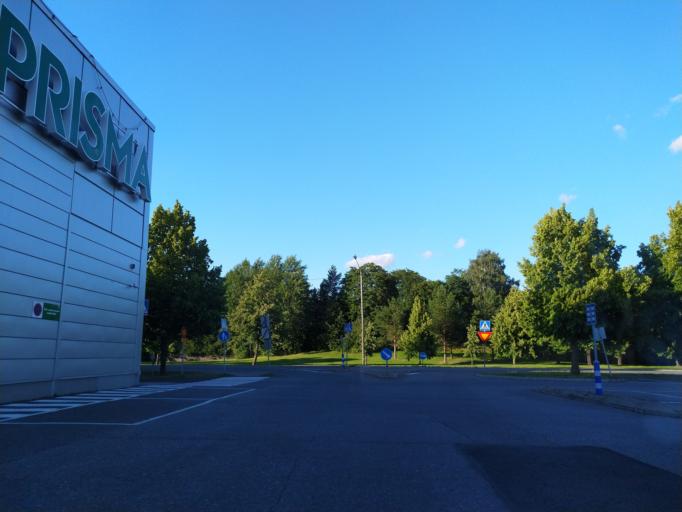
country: FI
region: Varsinais-Suomi
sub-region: Turku
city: Turku
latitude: 60.4461
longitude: 22.3247
